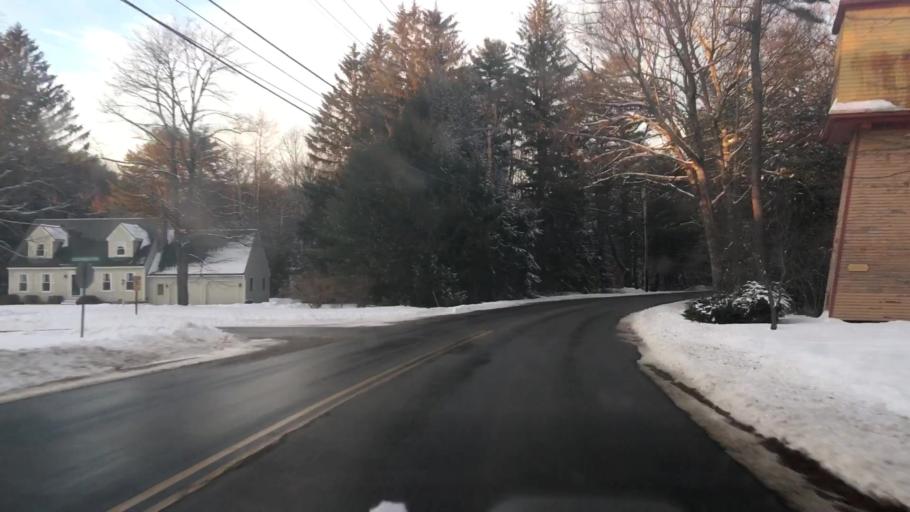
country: US
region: Maine
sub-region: Cumberland County
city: Brunswick
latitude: 43.9516
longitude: -69.9304
